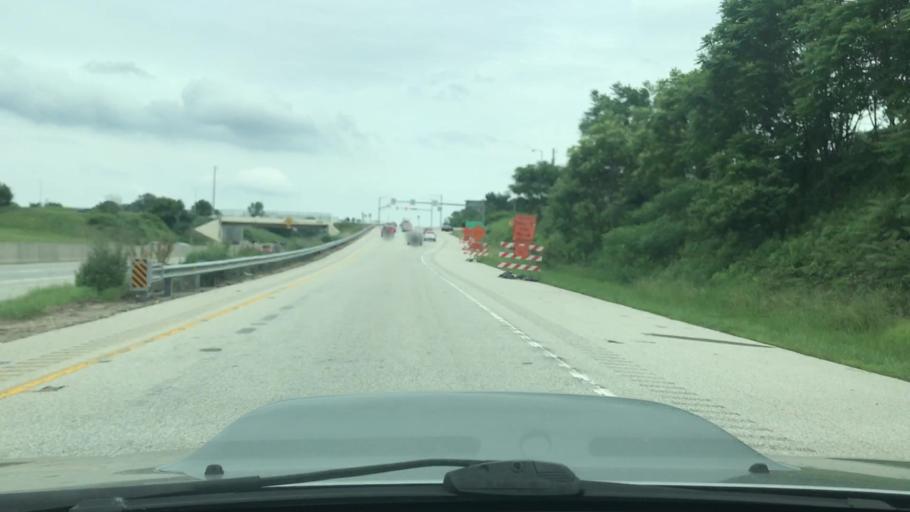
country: US
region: Pennsylvania
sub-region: Montgomery County
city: Wyncote
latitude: 40.0887
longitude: -75.1665
